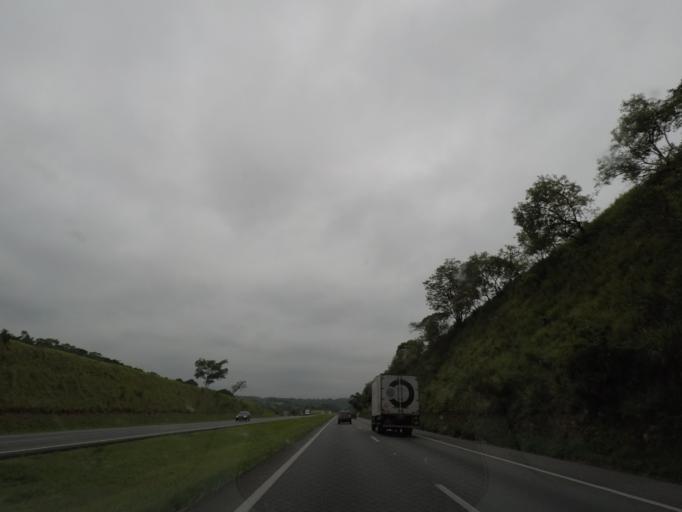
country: BR
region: Sao Paulo
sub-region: Jarinu
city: Jarinu
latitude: -23.0295
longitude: -46.7446
